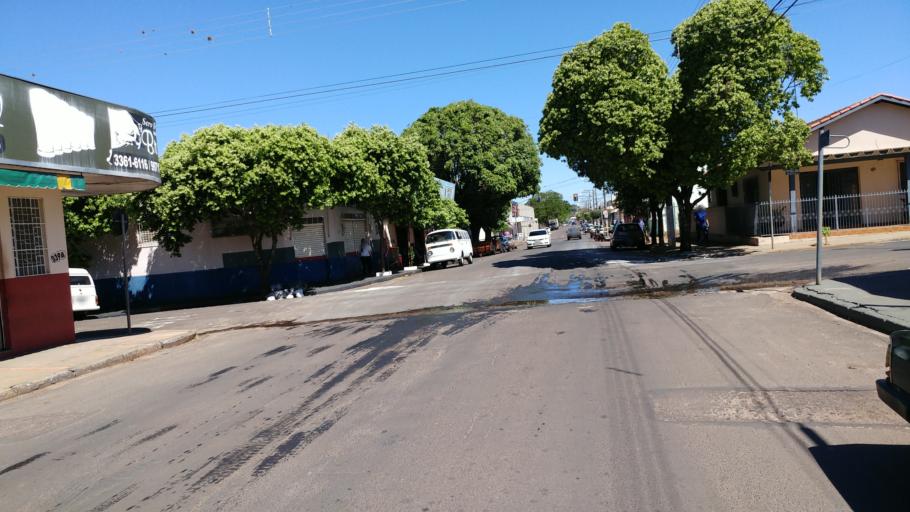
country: BR
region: Sao Paulo
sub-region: Paraguacu Paulista
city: Paraguacu Paulista
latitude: -22.4175
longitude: -50.5743
